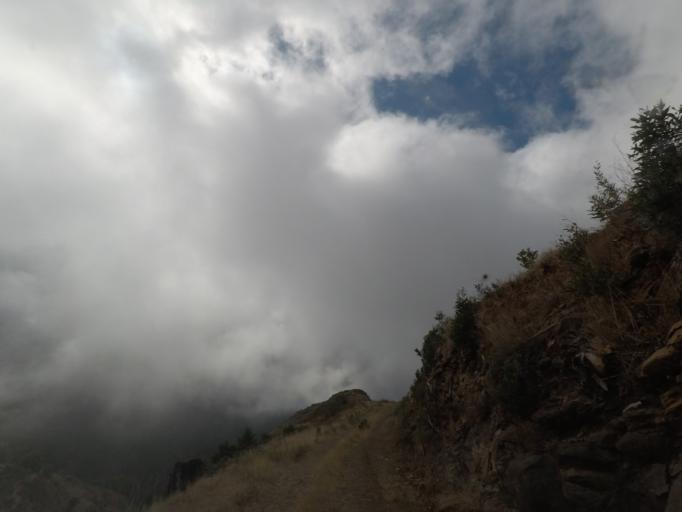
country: PT
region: Madeira
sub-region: Funchal
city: Nossa Senhora do Monte
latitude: 32.6970
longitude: -16.9123
